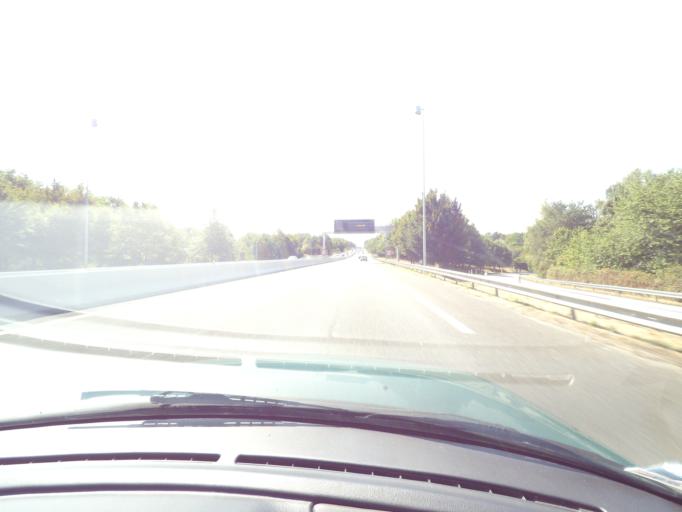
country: FR
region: Limousin
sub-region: Departement de la Haute-Vienne
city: Le Palais-sur-Vienne
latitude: 45.8750
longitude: 1.2878
